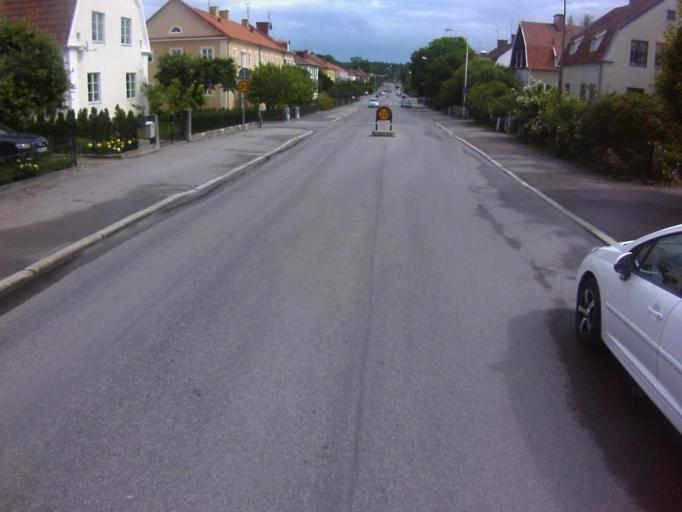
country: SE
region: Soedermanland
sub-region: Eskilstuna Kommun
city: Eskilstuna
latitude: 59.3618
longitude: 16.5189
